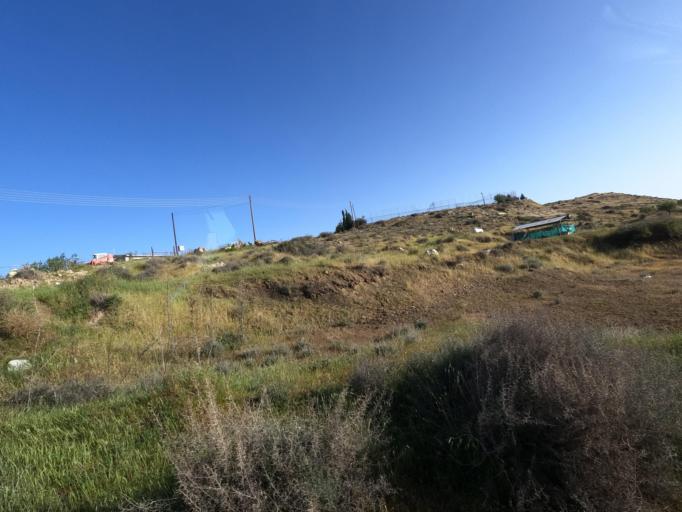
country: CY
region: Lefkosia
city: Astromeritis
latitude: 35.0778
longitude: 33.0216
